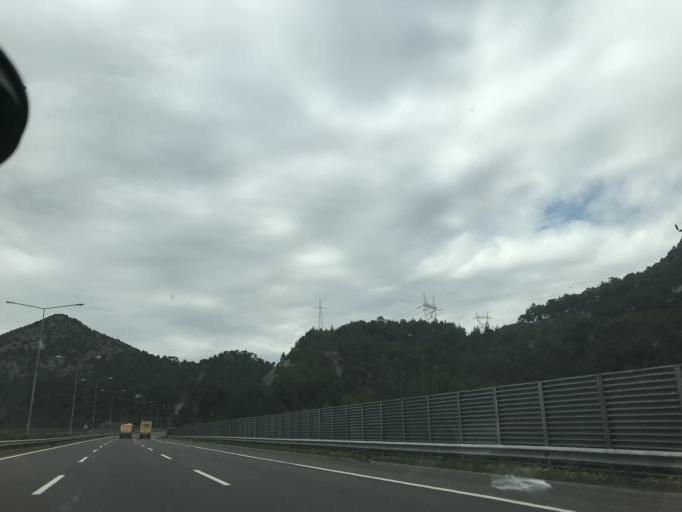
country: TR
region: Nigde
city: Ciftehan
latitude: 37.5025
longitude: 34.8238
